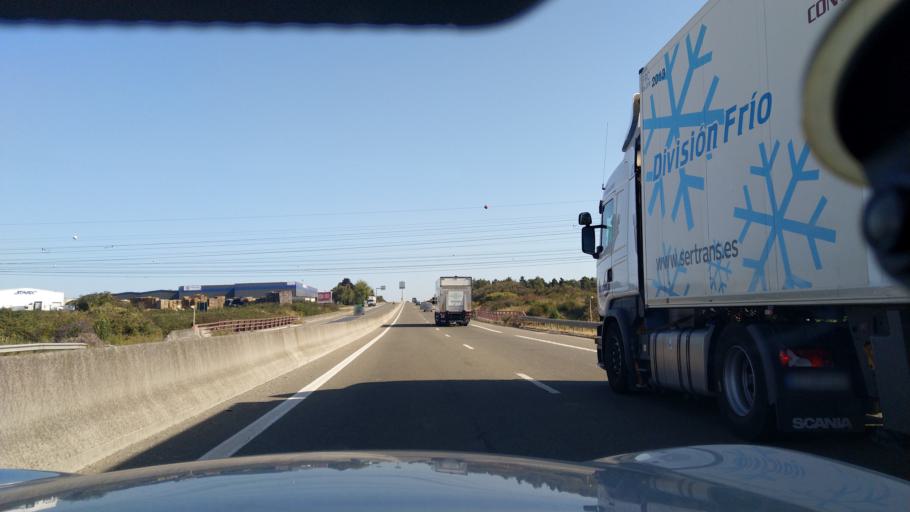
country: FR
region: Ile-de-France
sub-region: Departement du Val-d'Oise
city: Le Thillay
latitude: 48.9927
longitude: 2.4777
